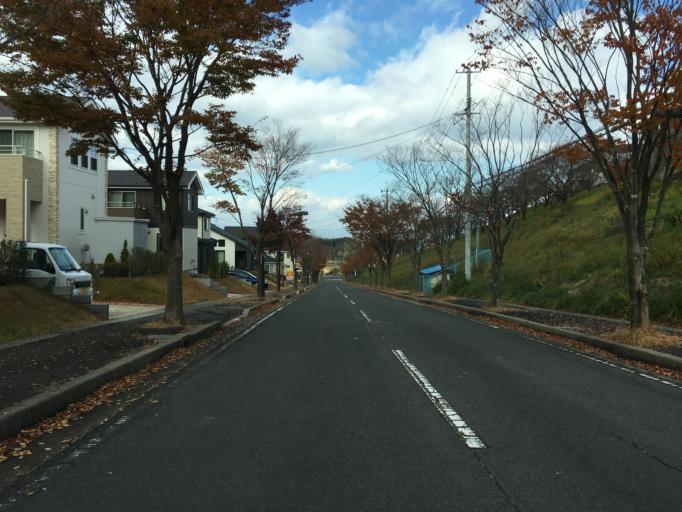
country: JP
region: Fukushima
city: Nihommatsu
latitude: 37.6625
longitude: 140.4659
